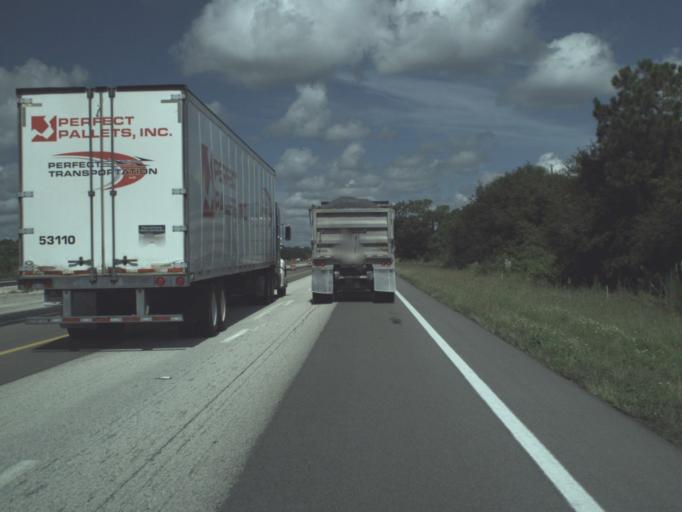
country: US
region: Florida
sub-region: Charlotte County
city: Port Charlotte
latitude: 27.0743
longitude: -82.1007
